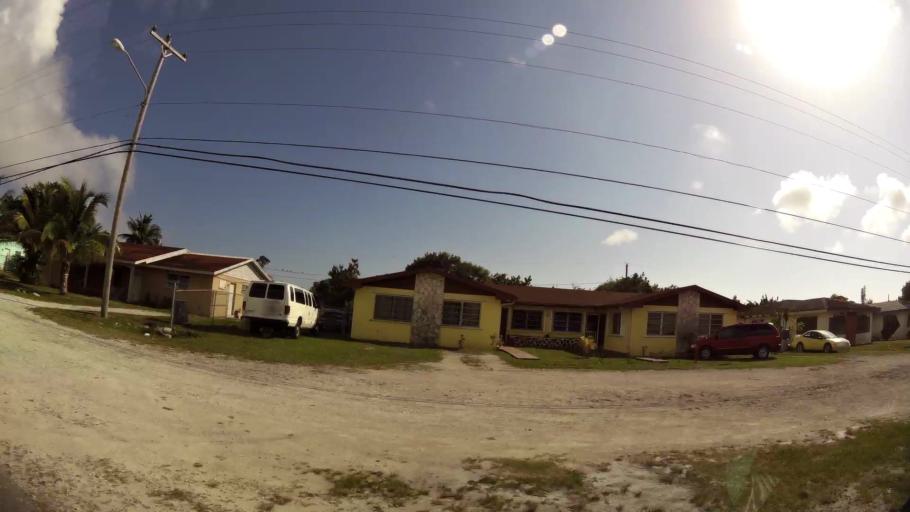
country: BS
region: Freeport
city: Freeport
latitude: 26.5221
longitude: -78.6877
